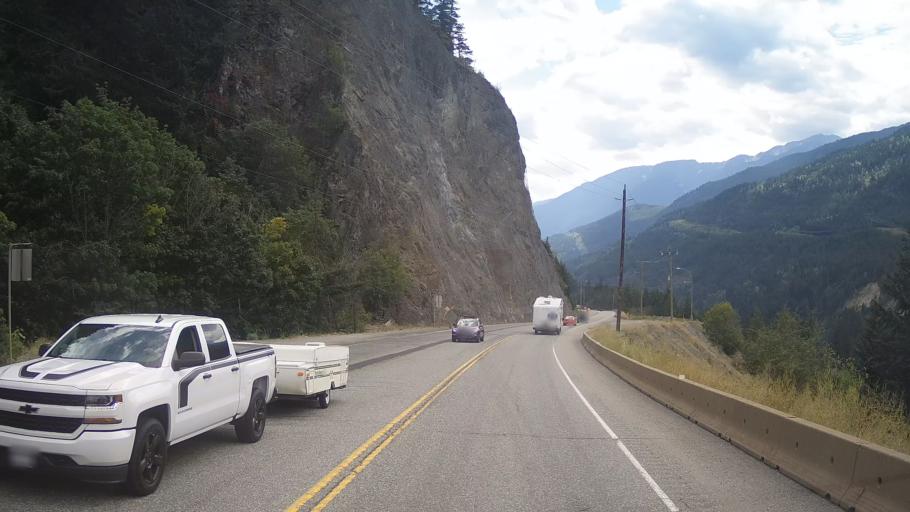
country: CA
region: British Columbia
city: Hope
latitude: 50.0665
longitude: -121.5450
